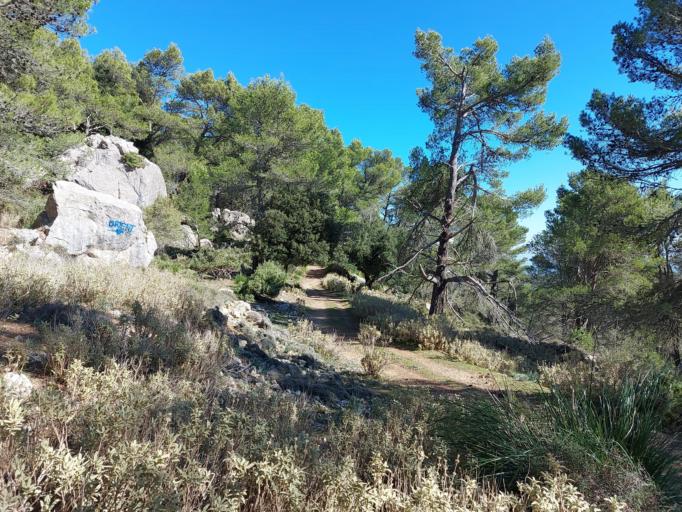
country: ES
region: Balearic Islands
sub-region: Illes Balears
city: Fornalutx
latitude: 39.7596
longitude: 2.7675
